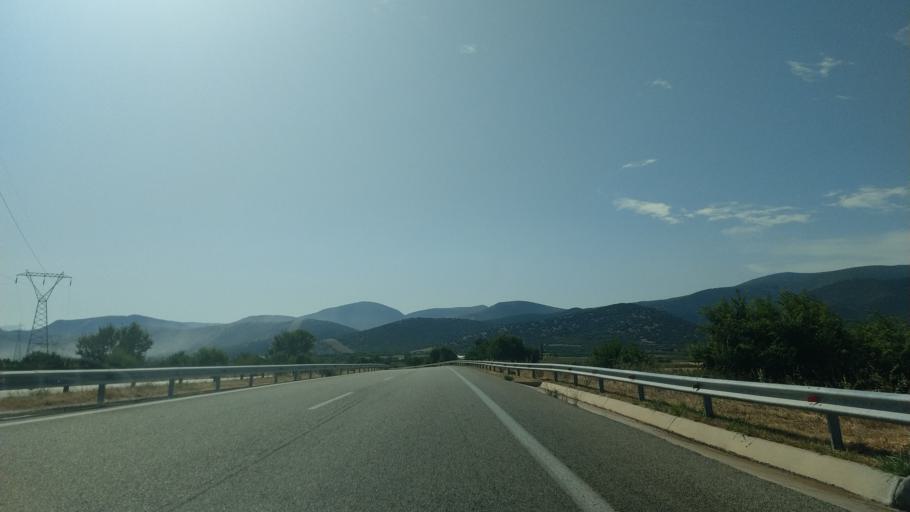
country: GR
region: East Macedonia and Thrace
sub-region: Nomos Kavalas
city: Nea Karvali
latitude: 40.9683
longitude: 24.5167
